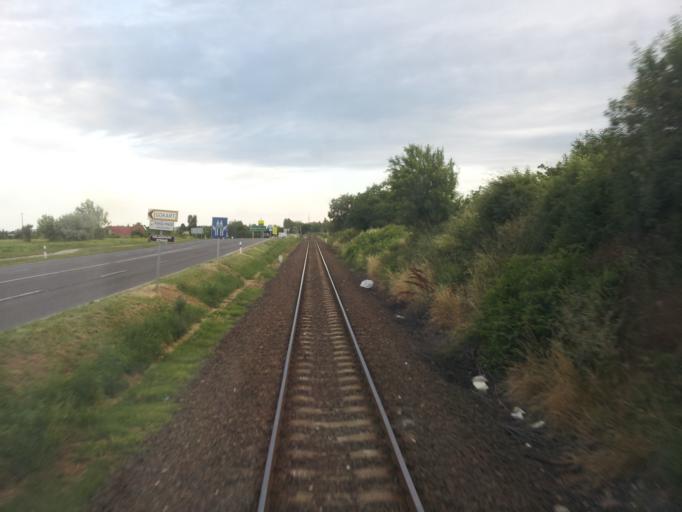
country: HU
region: Veszprem
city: Csopak
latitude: 46.9664
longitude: 17.9070
